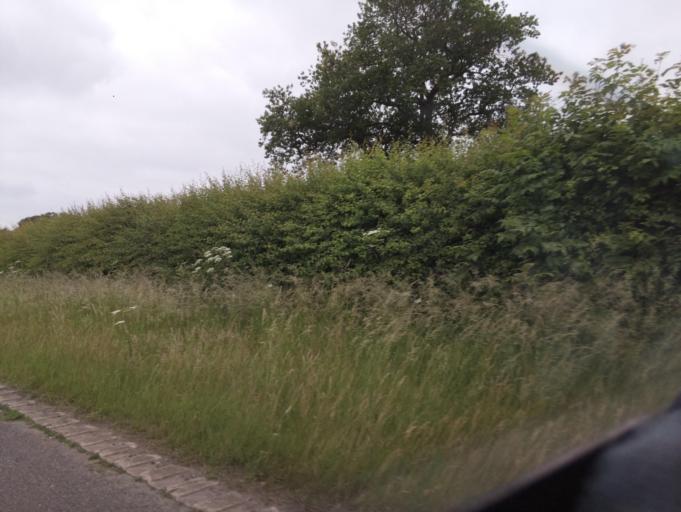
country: GB
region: England
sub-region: District of Rutland
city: Edith Weston
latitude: 52.6477
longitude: -0.6121
